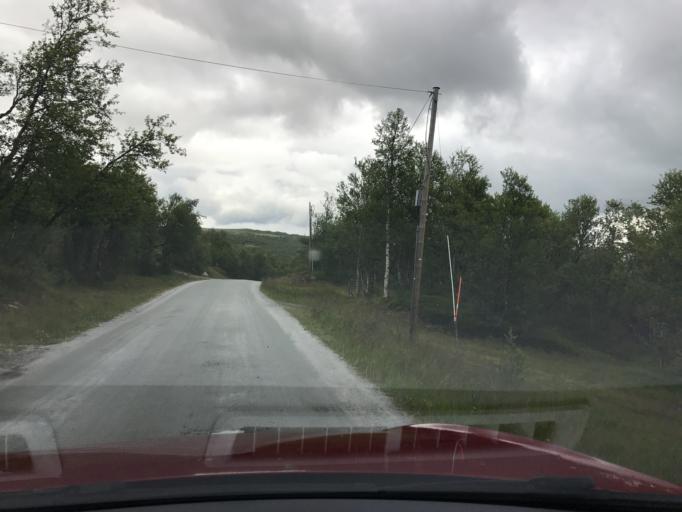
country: NO
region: Buskerud
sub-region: Hol
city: Geilo
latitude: 60.5495
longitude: 8.1983
